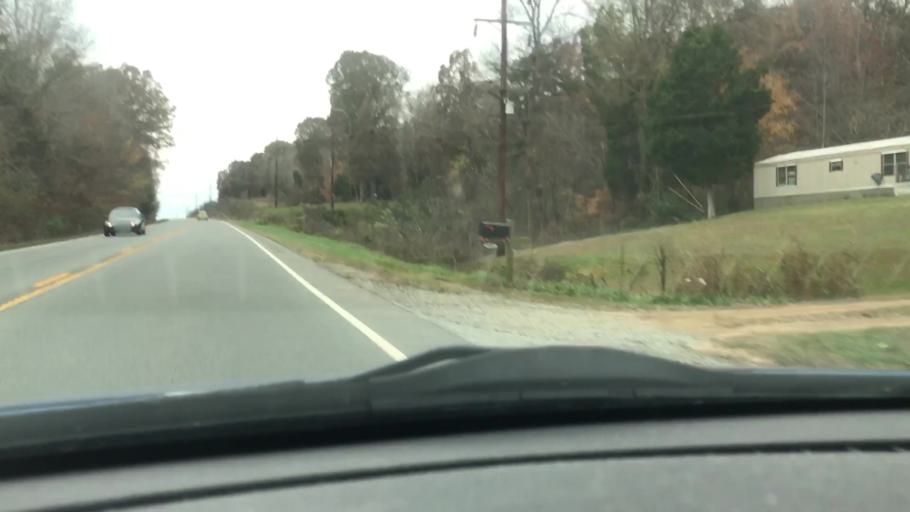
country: US
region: North Carolina
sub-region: Davidson County
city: Thomasville
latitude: 35.7635
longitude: -80.0698
